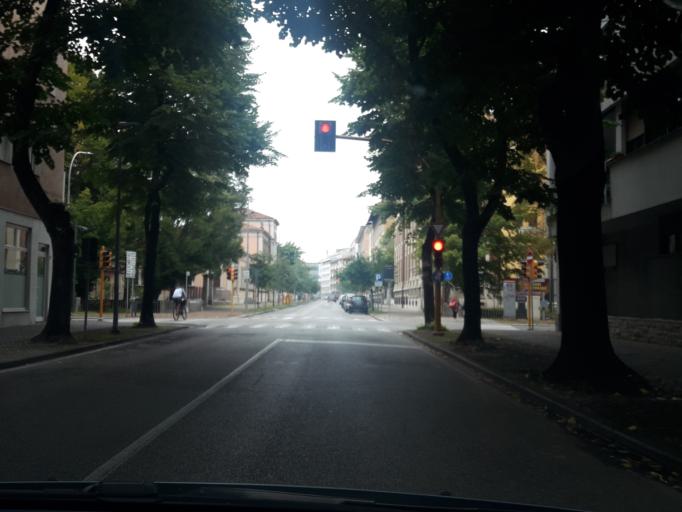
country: IT
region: Friuli Venezia Giulia
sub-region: Provincia di Udine
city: Udine
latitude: 46.0573
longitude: 13.2383
